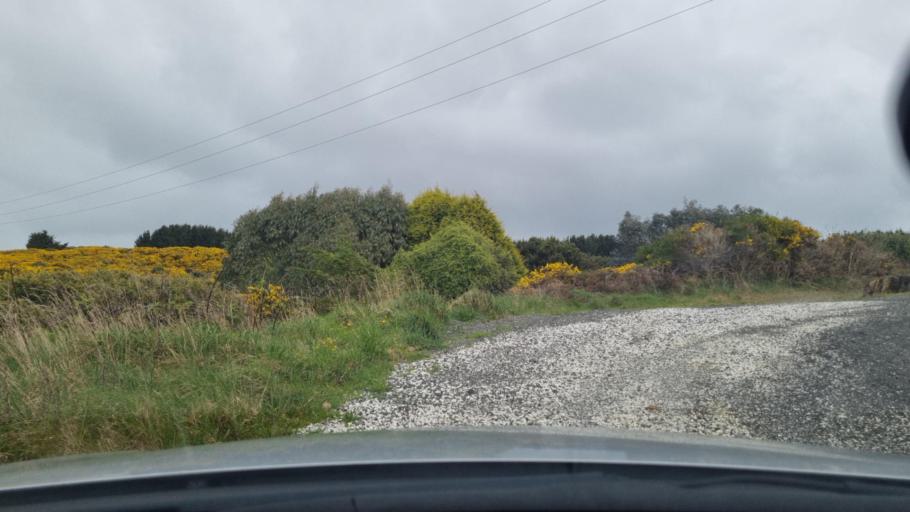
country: NZ
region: Southland
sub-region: Invercargill City
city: Bluff
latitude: -46.5767
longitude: 168.2982
